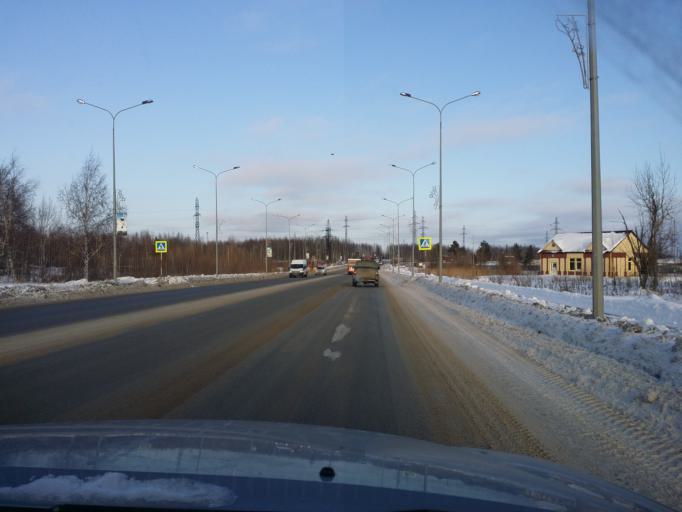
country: RU
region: Khanty-Mansiyskiy Avtonomnyy Okrug
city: Megion
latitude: 61.0435
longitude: 76.1079
